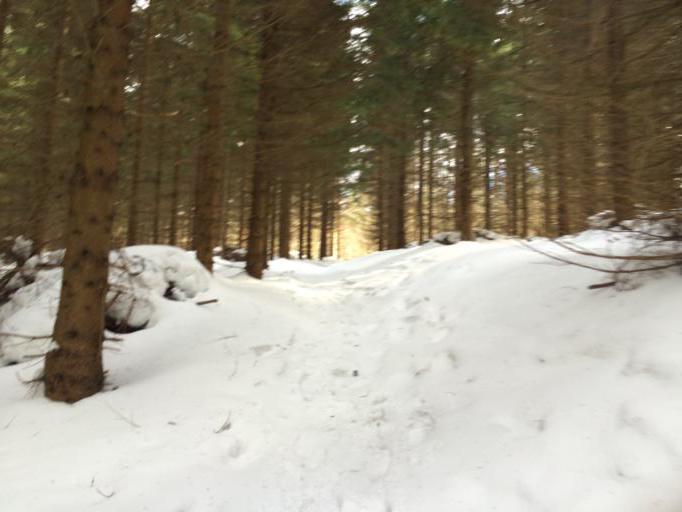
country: CZ
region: Olomoucky
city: Vapenna
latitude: 50.2603
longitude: 17.0082
